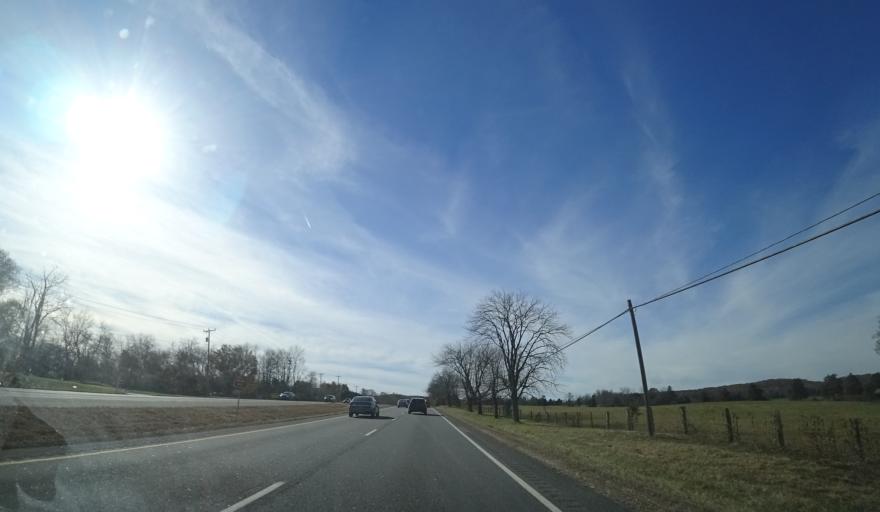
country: US
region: Virginia
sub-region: Fauquier County
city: New Baltimore
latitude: 38.7713
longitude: -77.6983
